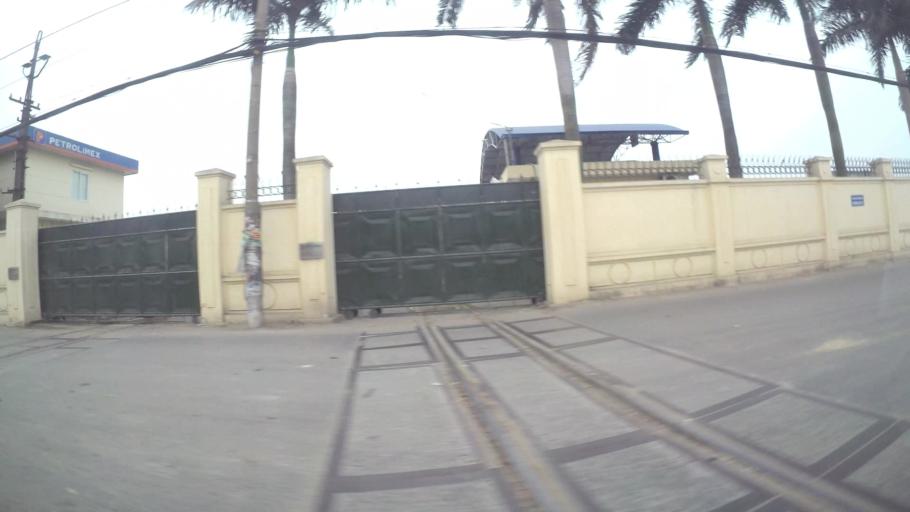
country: VN
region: Ha Noi
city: Hoan Kiem
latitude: 21.0659
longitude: 105.8926
